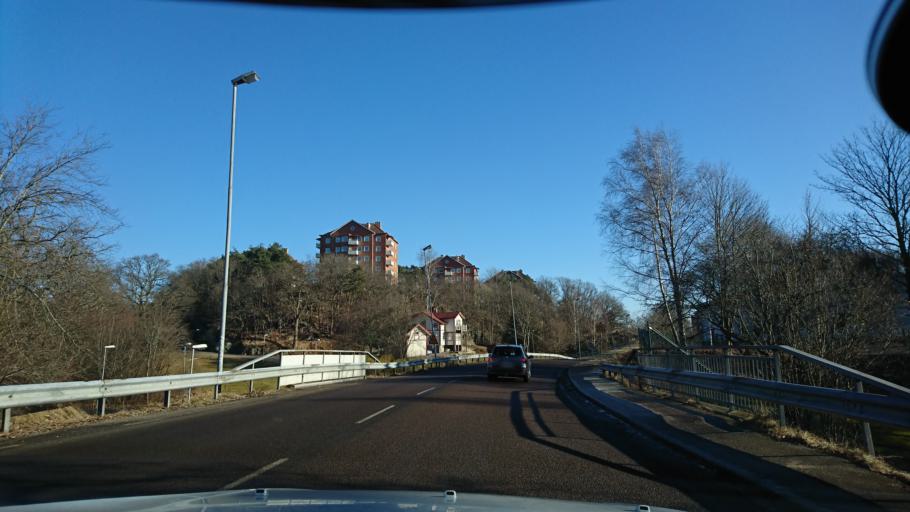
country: SE
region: Vaestra Goetaland
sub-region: Uddevalla Kommun
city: Uddevalla
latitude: 58.3577
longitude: 11.9217
